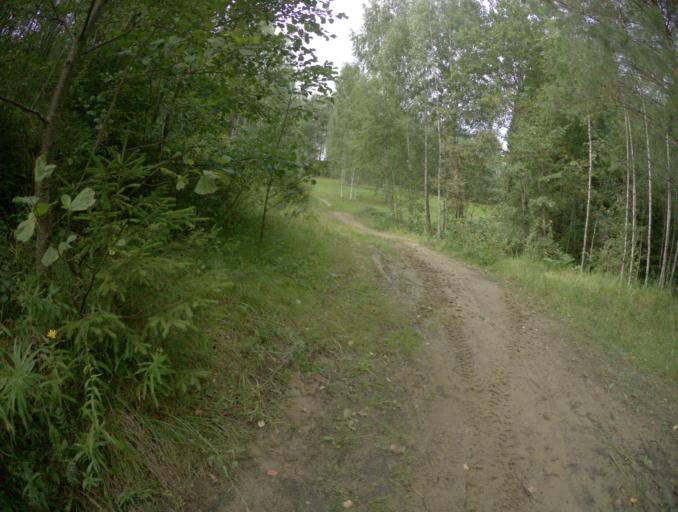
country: RU
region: Vladimir
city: Raduzhnyy
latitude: 56.0047
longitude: 40.3173
